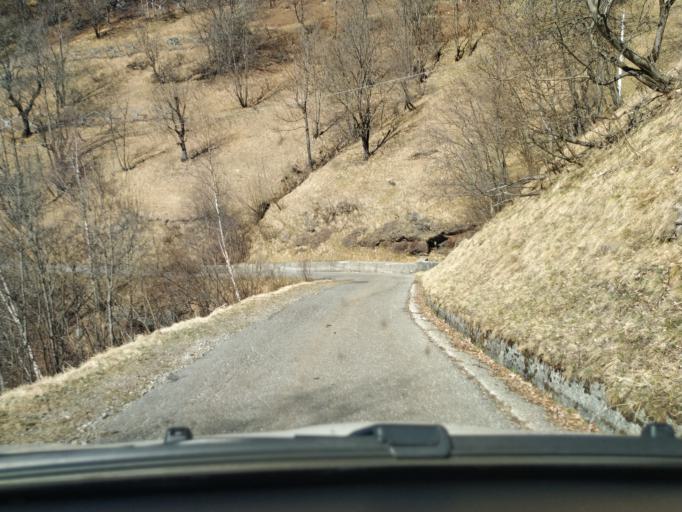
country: IT
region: Piedmont
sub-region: Provincia di Vercelli
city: Rimella
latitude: 45.9082
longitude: 8.1915
